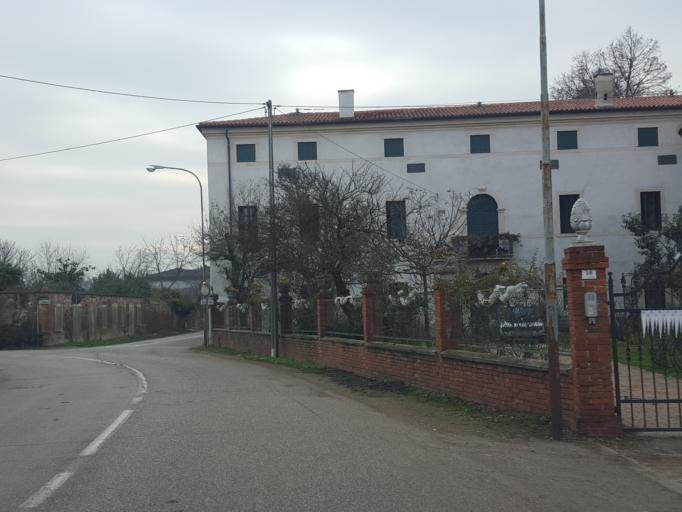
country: IT
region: Veneto
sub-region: Provincia di Verona
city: Arcole
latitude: 45.3555
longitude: 11.2800
